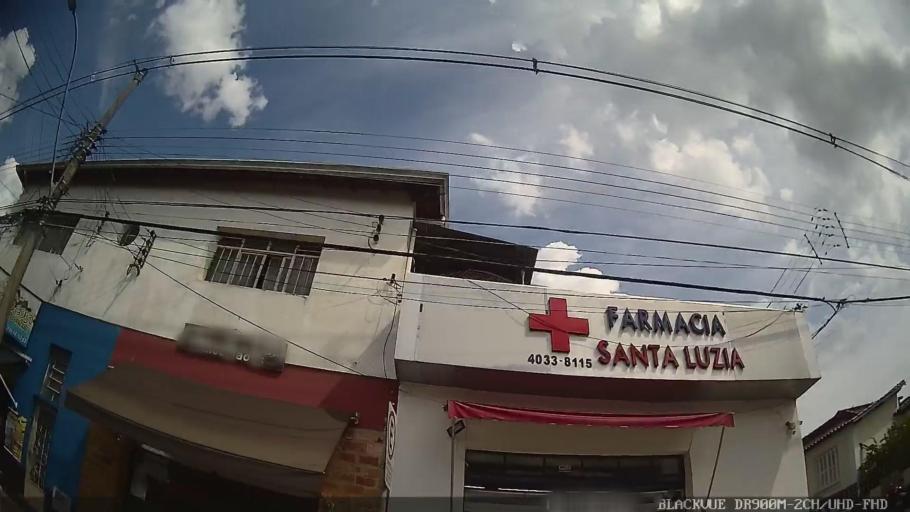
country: BR
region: Sao Paulo
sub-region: Braganca Paulista
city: Braganca Paulista
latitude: -22.9686
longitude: -46.5457
